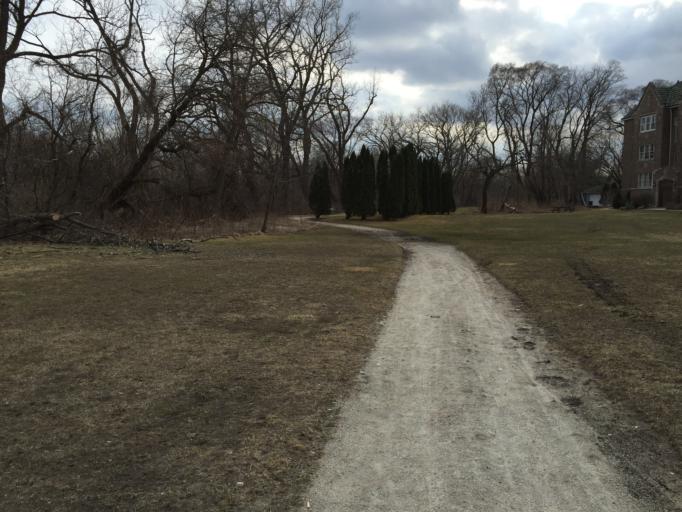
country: US
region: Illinois
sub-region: Cook County
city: Evanston
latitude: 42.0639
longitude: -87.6881
